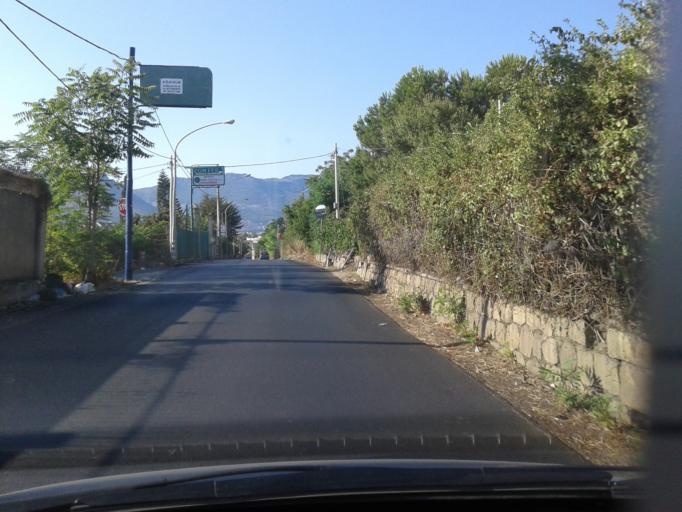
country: IT
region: Sicily
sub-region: Palermo
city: Monreale
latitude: 38.0996
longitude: 13.3100
